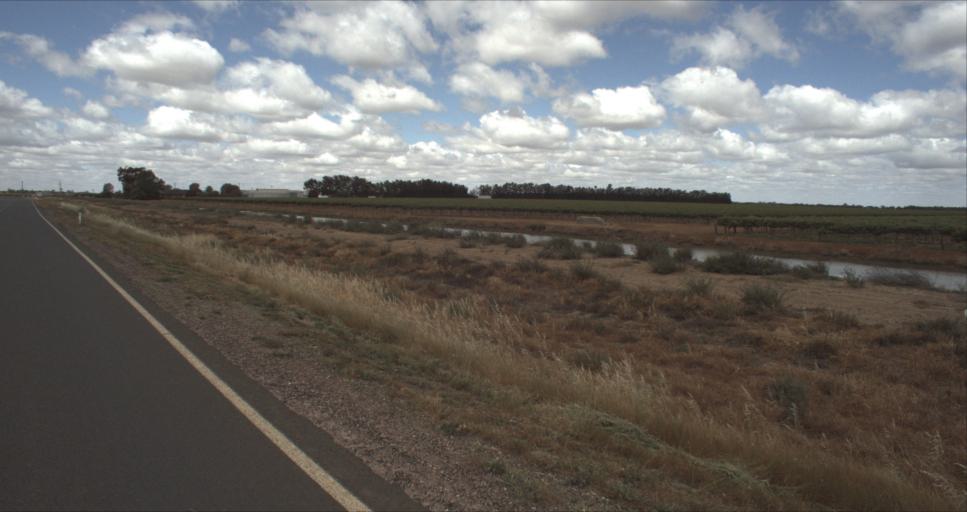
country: AU
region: New South Wales
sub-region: Murrumbidgee Shire
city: Darlington Point
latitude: -34.4919
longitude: 146.1657
